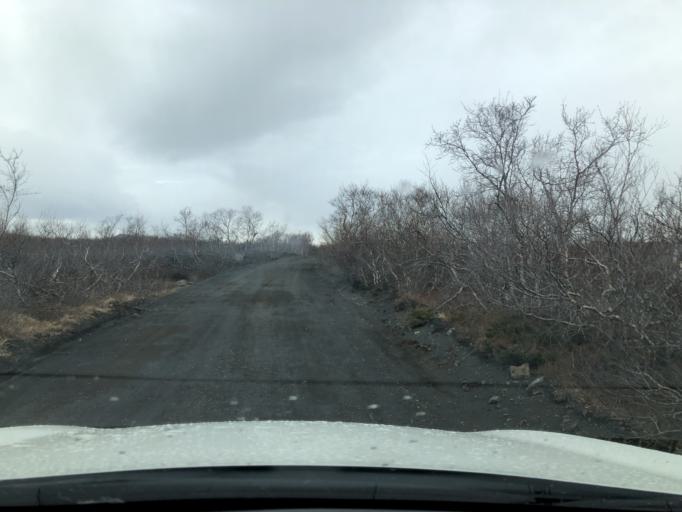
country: IS
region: Northeast
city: Laugar
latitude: 65.6073
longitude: -16.8970
